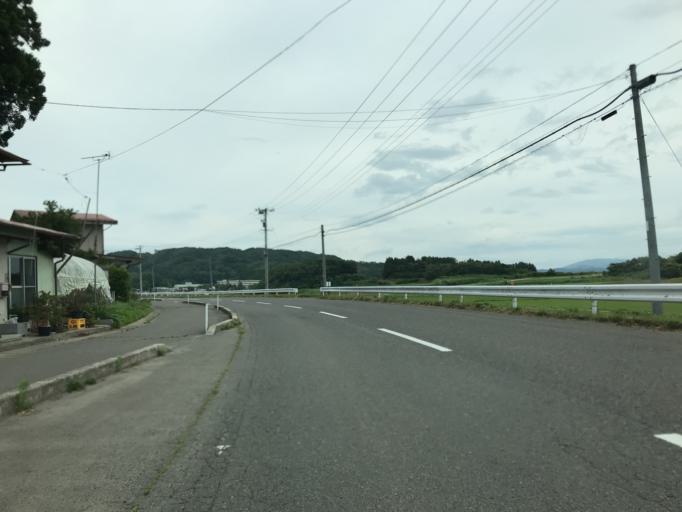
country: JP
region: Fukushima
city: Funehikimachi-funehiki
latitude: 37.3911
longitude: 140.5625
